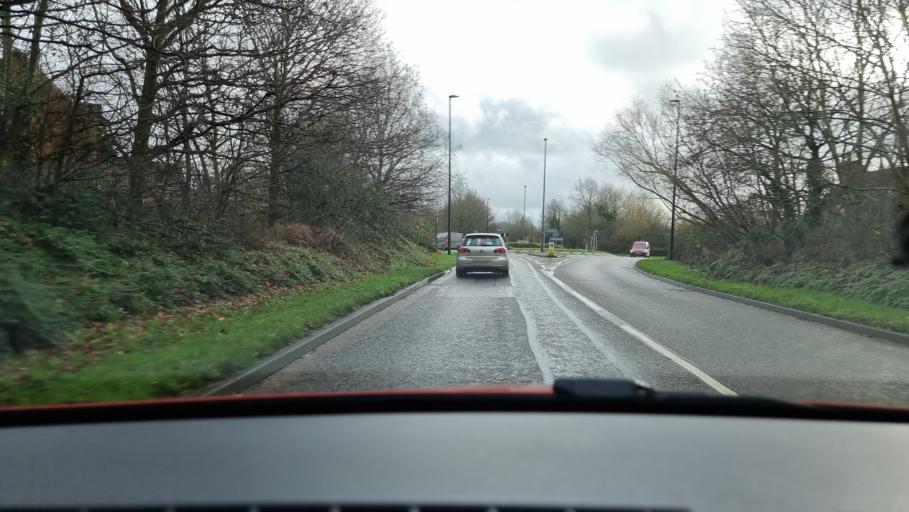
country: GB
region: England
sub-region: Buckinghamshire
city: Aylesbury
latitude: 51.8128
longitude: -0.8375
